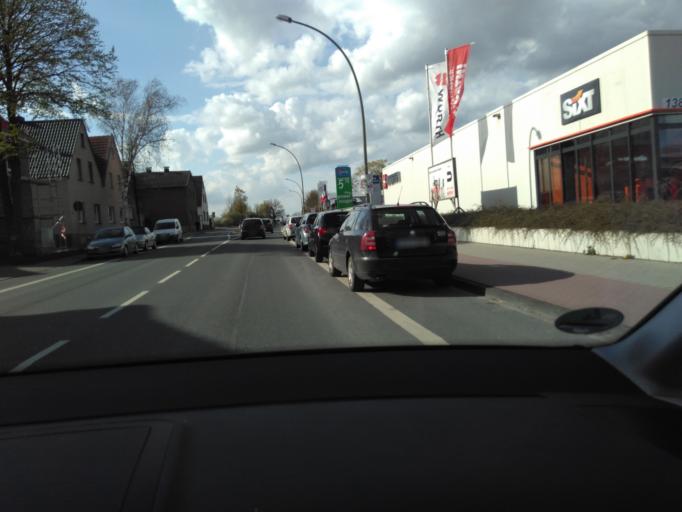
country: DE
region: North Rhine-Westphalia
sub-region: Regierungsbezirk Munster
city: Beckum
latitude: 51.7719
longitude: 8.0377
